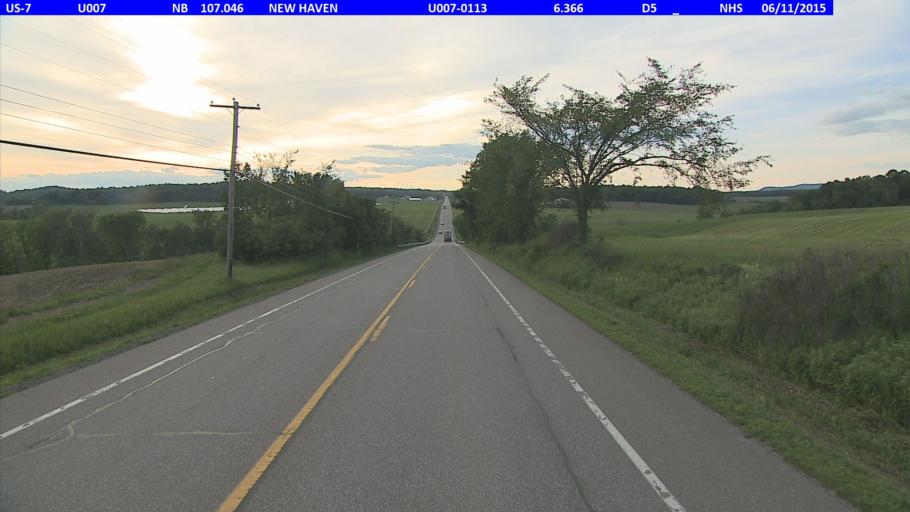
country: US
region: Vermont
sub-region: Addison County
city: Vergennes
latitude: 44.1342
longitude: -73.1929
